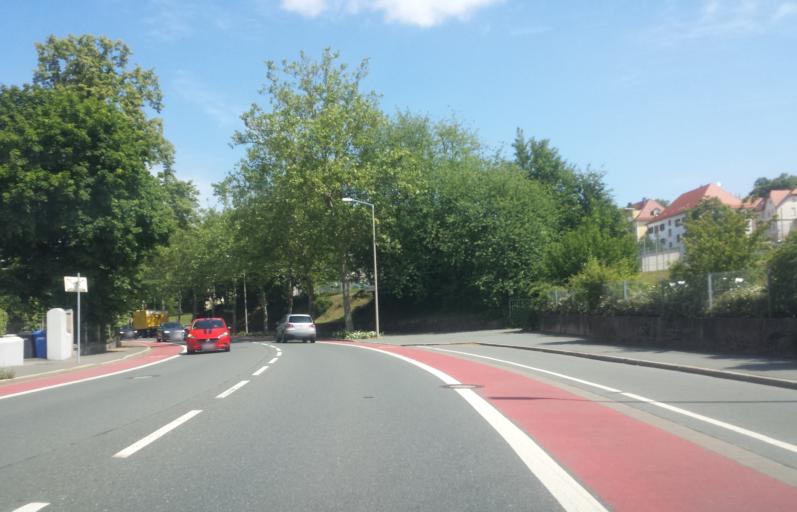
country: DE
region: Bavaria
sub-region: Upper Franconia
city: Kulmbach
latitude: 50.1015
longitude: 11.4469
